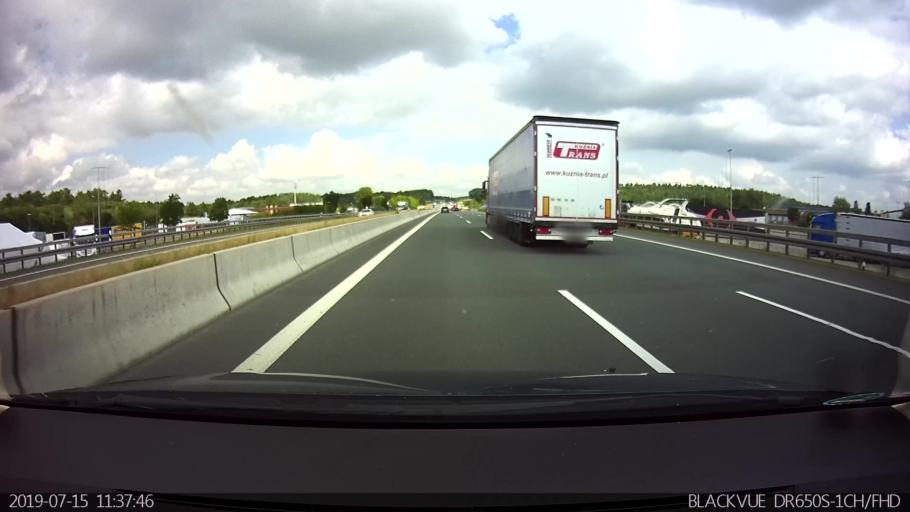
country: DE
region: Bavaria
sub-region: Upper Franconia
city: Pegnitz
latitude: 49.7484
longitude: 11.5123
